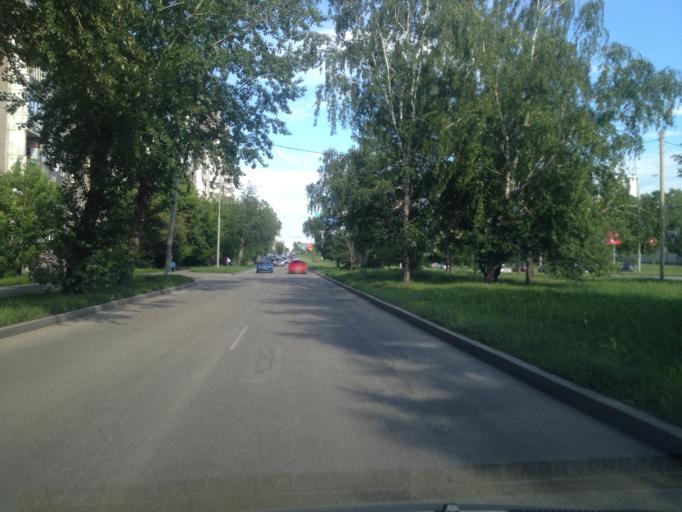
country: RU
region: Sverdlovsk
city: Shirokaya Rechka
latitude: 56.8271
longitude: 60.5383
